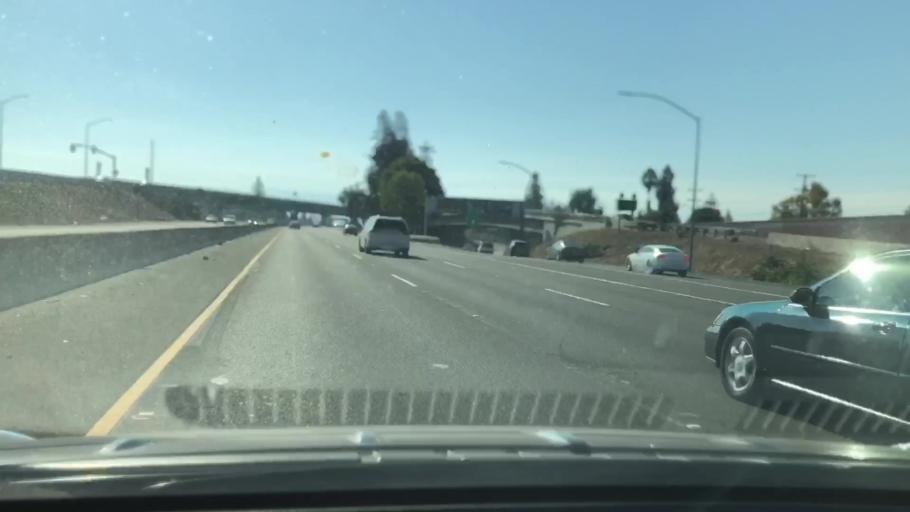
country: US
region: California
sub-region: Santa Clara County
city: Burbank
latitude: 37.3211
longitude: -121.9405
